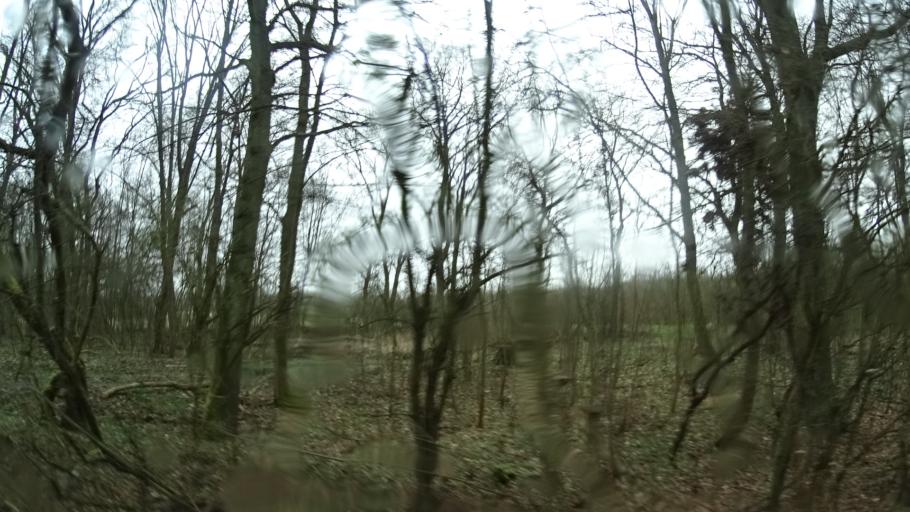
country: DE
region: Hesse
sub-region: Regierungsbezirk Darmstadt
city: Stockstadt am Rhein
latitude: 49.8308
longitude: 8.4192
